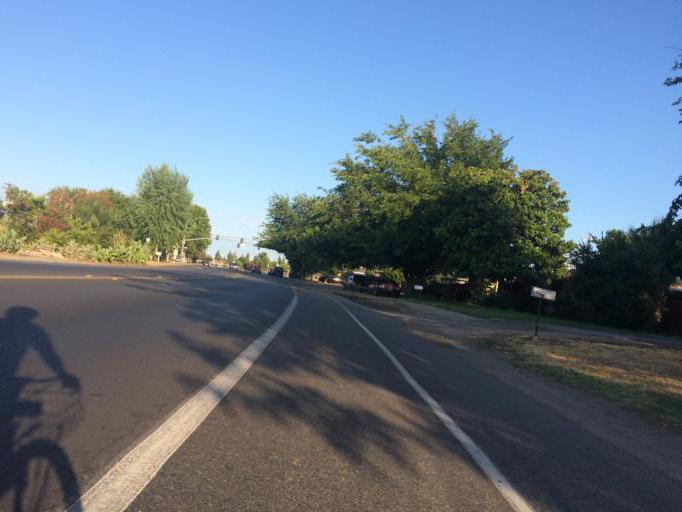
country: US
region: California
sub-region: Fresno County
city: Tarpey Village
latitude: 36.7944
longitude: -119.7075
